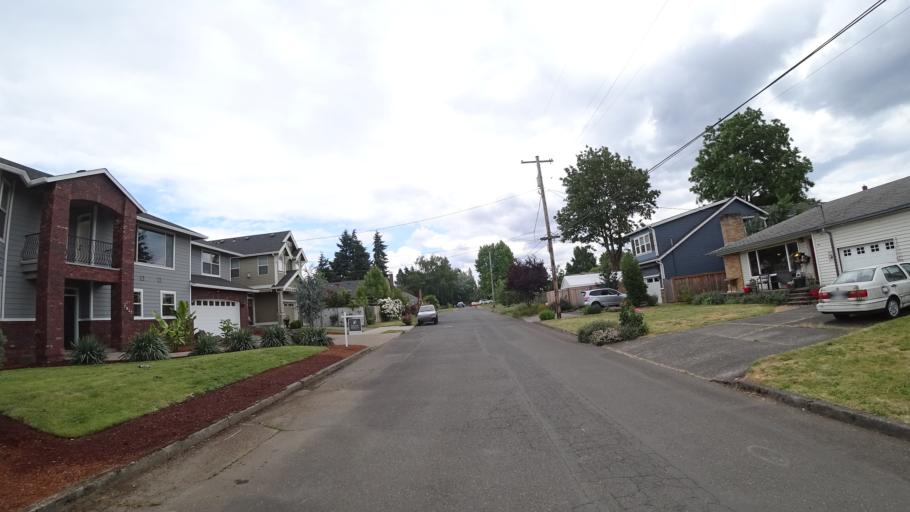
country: US
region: Oregon
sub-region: Washington County
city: West Haven
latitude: 45.5842
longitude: -122.7507
